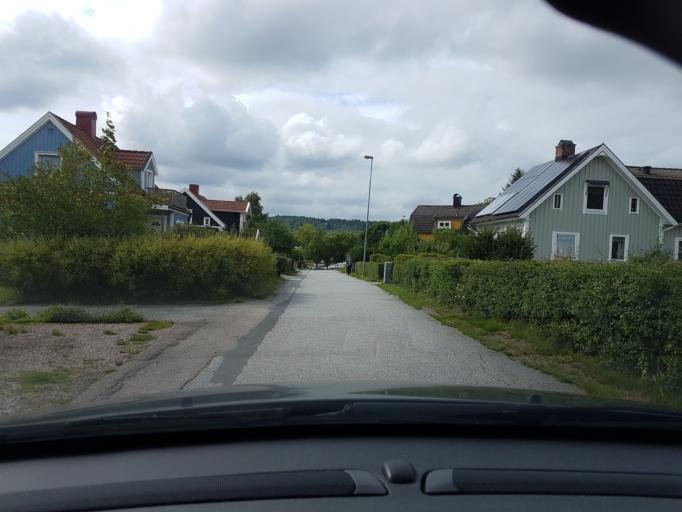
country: SE
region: Vaestra Goetaland
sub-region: Ale Kommun
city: Alafors
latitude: 57.9162
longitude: 12.0693
